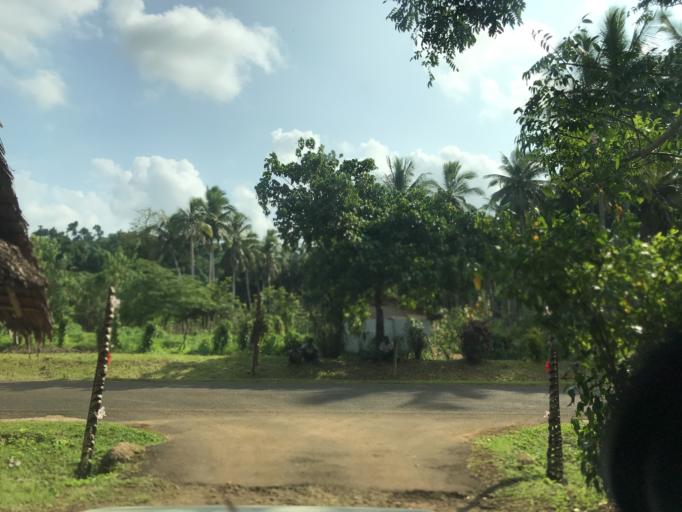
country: VU
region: Sanma
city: Luganville
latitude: -15.3130
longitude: 167.1664
